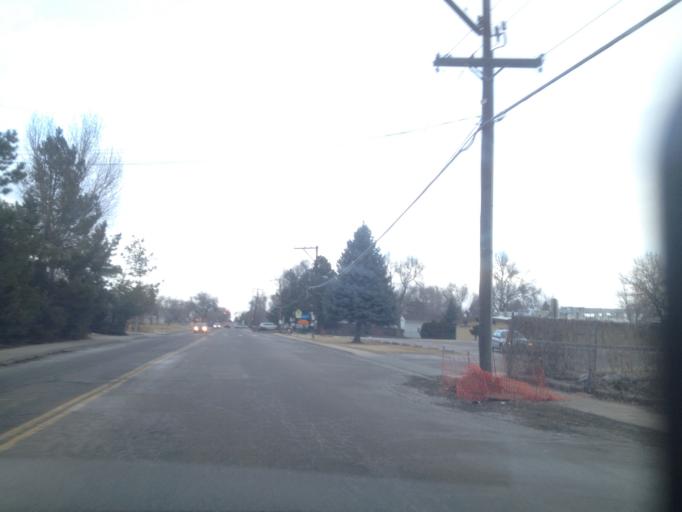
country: US
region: Colorado
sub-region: Adams County
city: Berkley
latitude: 39.8108
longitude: -105.0441
